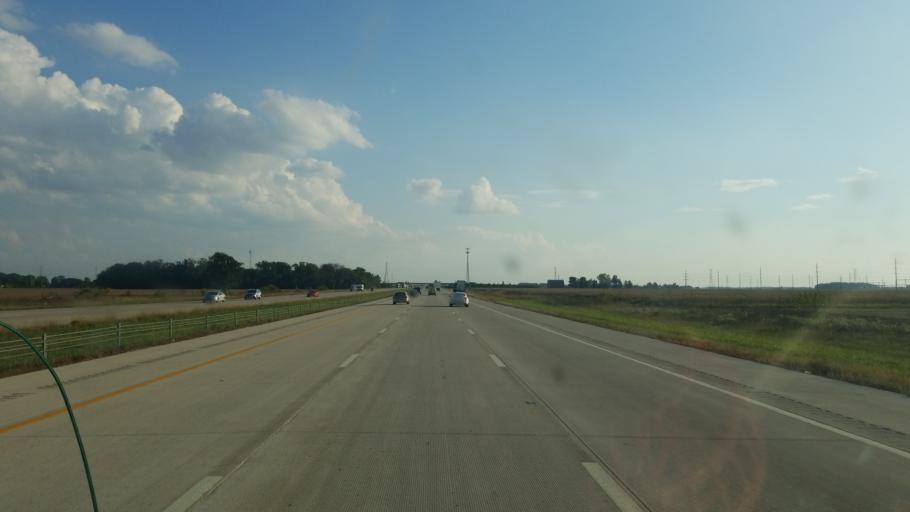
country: US
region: Ohio
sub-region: Wood County
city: Perrysburg
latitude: 41.4864
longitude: -83.6223
